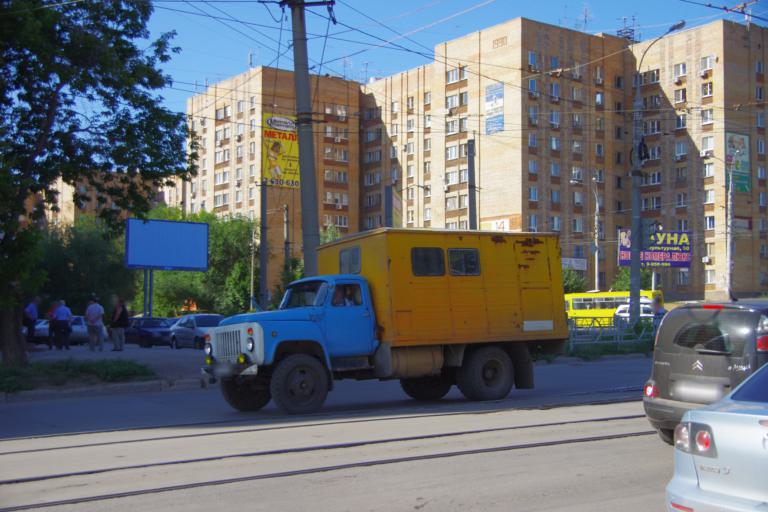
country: RU
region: Samara
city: Samara
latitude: 53.1968
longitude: 50.1562
